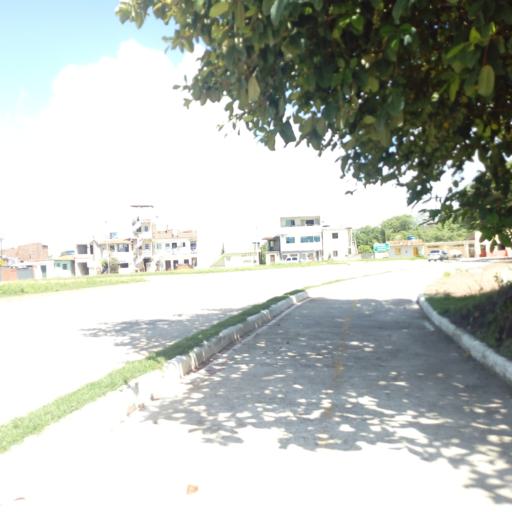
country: BR
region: Pernambuco
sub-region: Sirinhaem
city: Sirinhaem
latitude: -8.5250
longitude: -35.0101
